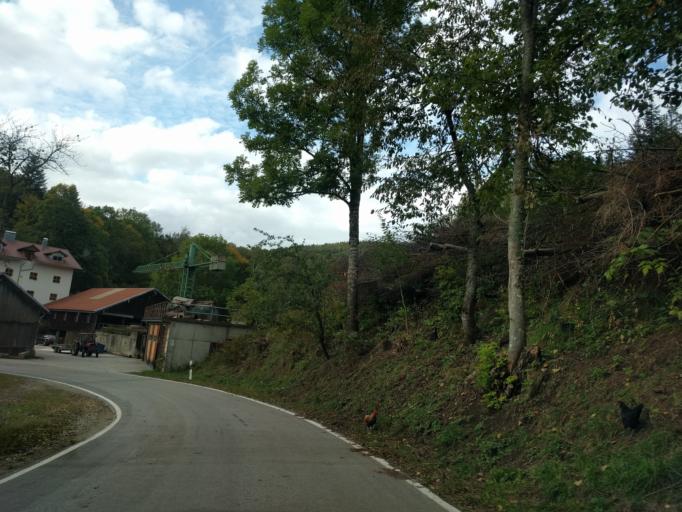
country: DE
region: Bavaria
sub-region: Lower Bavaria
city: Grafling
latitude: 48.8844
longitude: 13.0080
